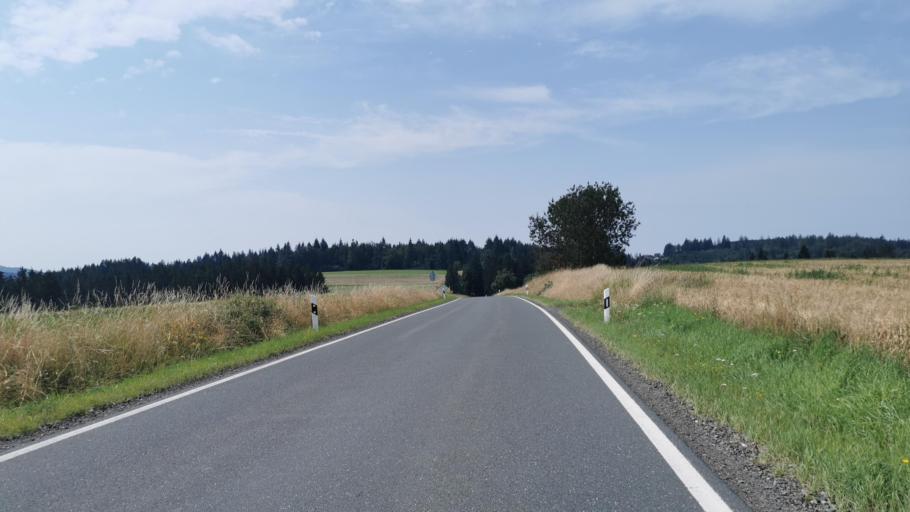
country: DE
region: Bavaria
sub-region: Upper Franconia
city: Wilhelmsthal
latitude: 50.3107
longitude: 11.4033
